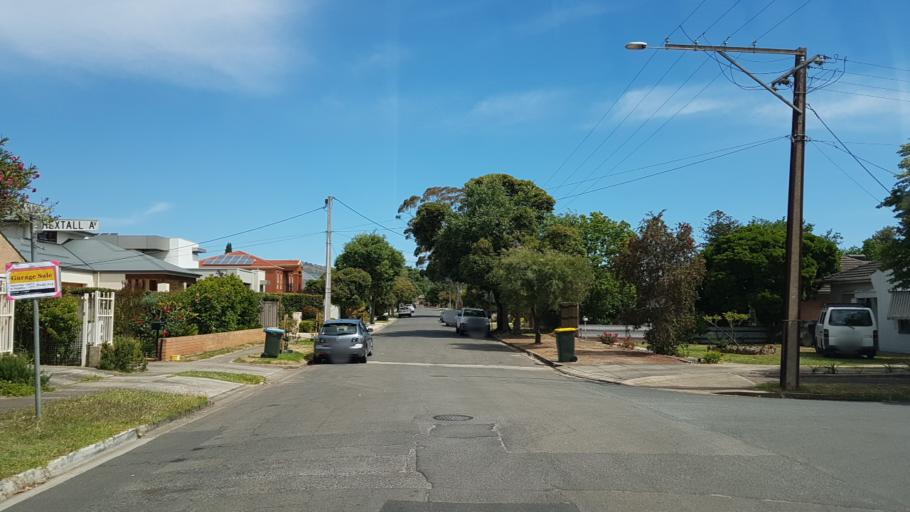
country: AU
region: South Australia
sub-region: Burnside
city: Kensington Gardens
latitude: -34.9112
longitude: 138.6650
